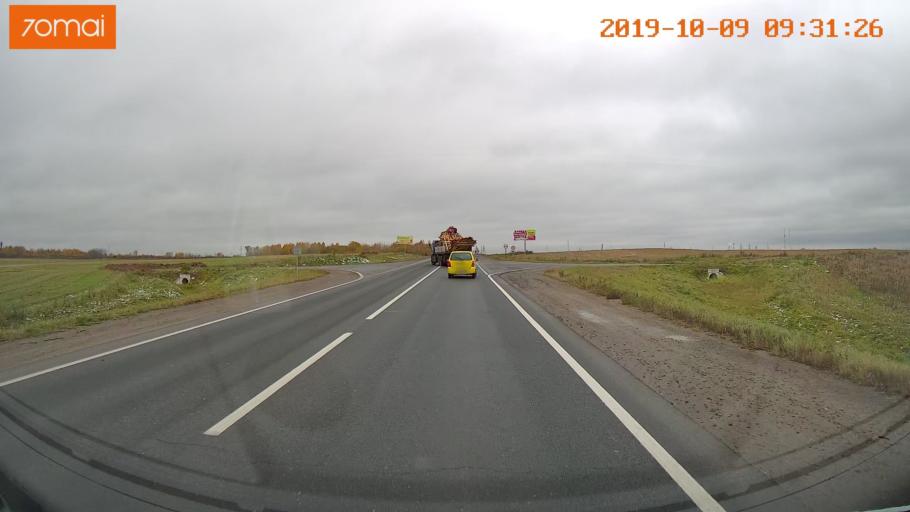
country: RU
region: Vologda
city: Vologda
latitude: 59.1496
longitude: 39.9386
